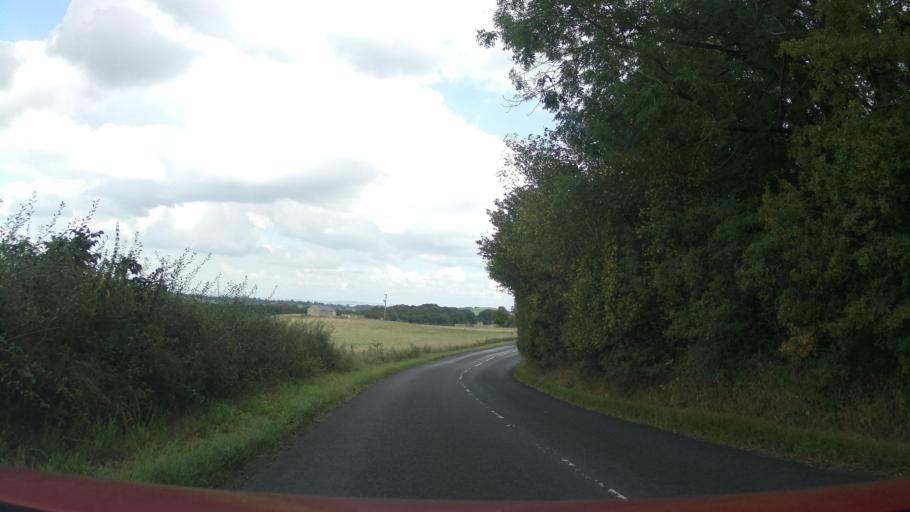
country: GB
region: England
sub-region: North Yorkshire
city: Catterick Garrison
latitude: 54.2564
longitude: -1.7147
